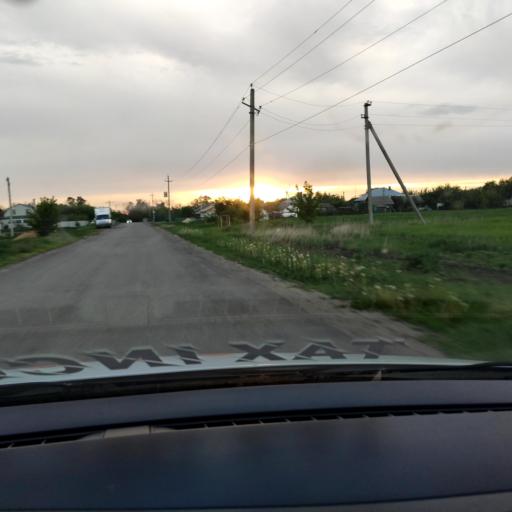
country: RU
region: Voronezj
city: Maslovka
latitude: 51.4477
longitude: 39.2384
